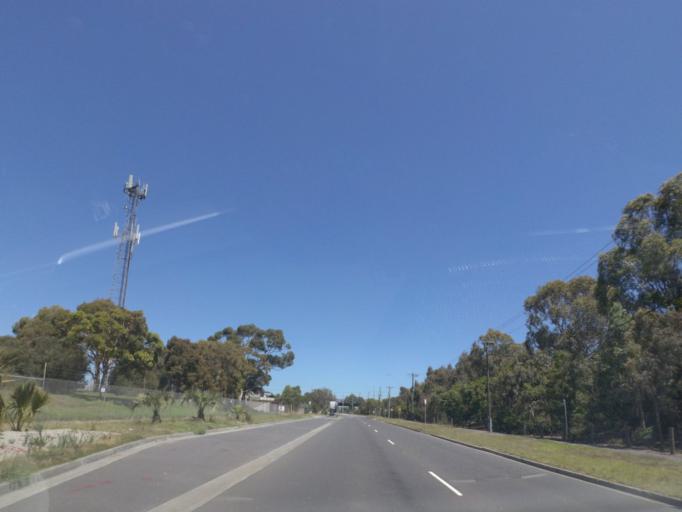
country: AU
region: Victoria
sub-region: Maribyrnong
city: Yarraville
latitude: -37.8297
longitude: 144.9118
